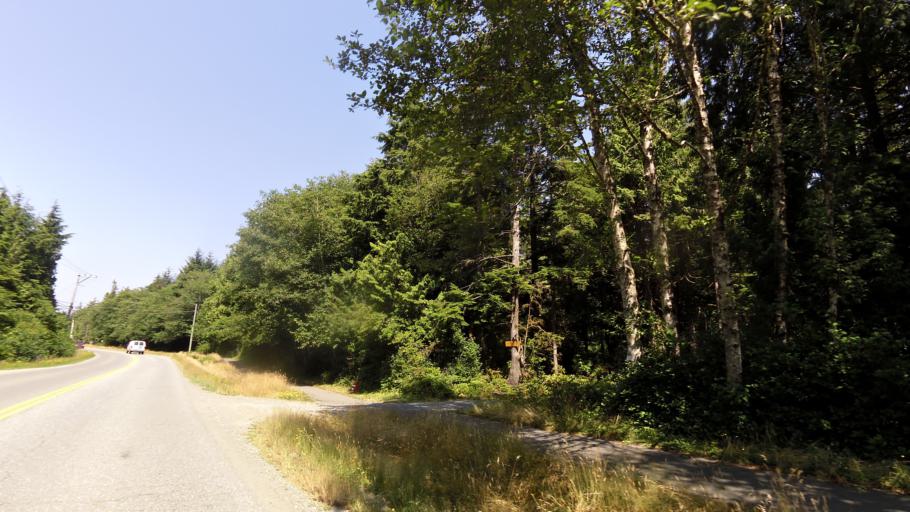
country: CA
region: British Columbia
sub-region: Regional District of Alberni-Clayoquot
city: Tofino
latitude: 49.1195
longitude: -125.8876
